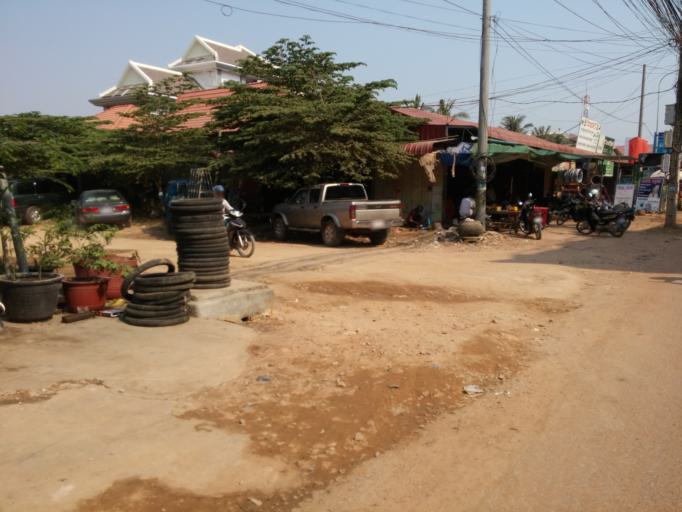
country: KH
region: Siem Reap
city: Siem Reap
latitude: 13.3799
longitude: 103.8518
